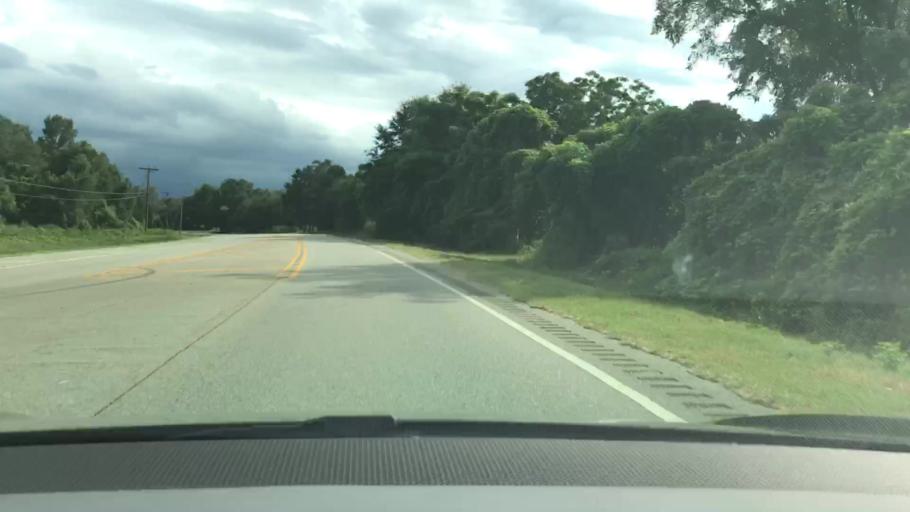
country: US
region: Alabama
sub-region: Coffee County
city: Elba
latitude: 31.5653
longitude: -86.0124
